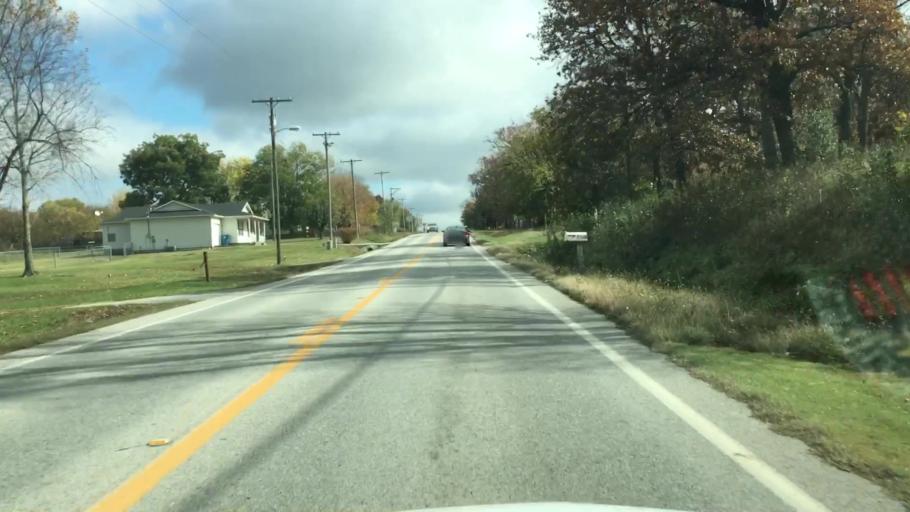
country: US
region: Arkansas
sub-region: Benton County
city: Gentry
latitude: 36.2637
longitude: -94.4694
